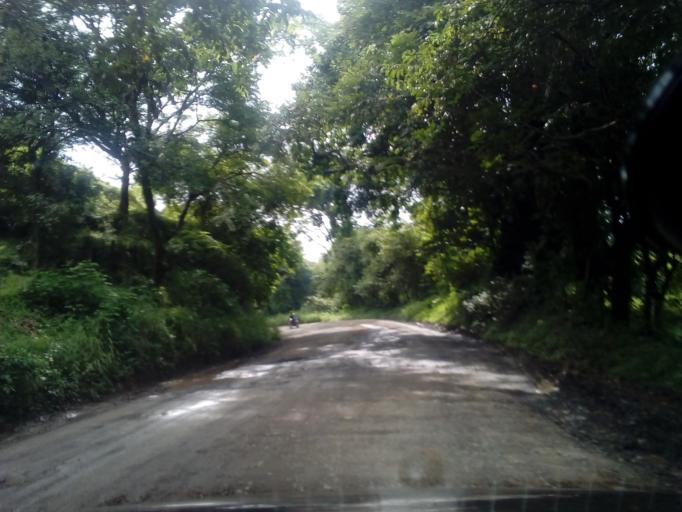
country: CR
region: Guanacaste
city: Samara
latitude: 9.9259
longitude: -85.6575
